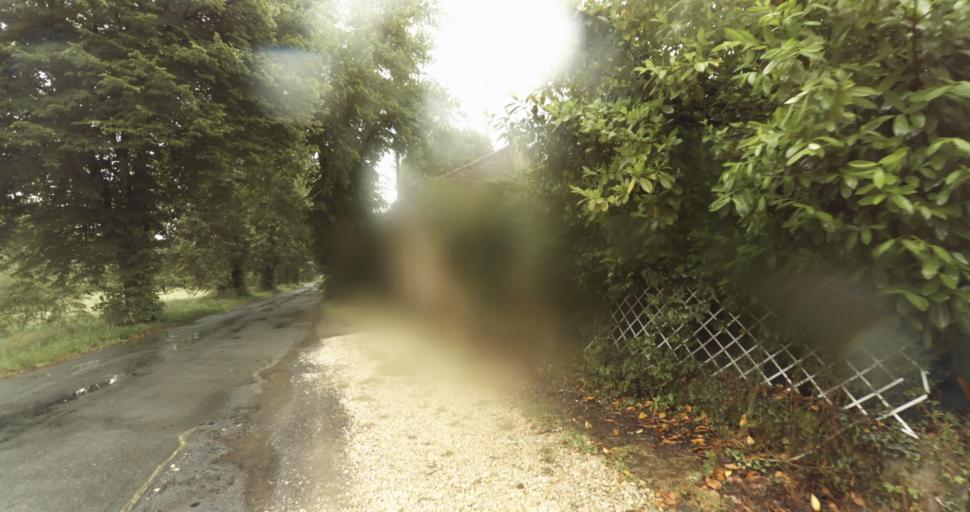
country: FR
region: Aquitaine
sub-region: Departement de la Dordogne
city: Beaumont-du-Perigord
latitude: 44.8121
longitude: 0.8668
